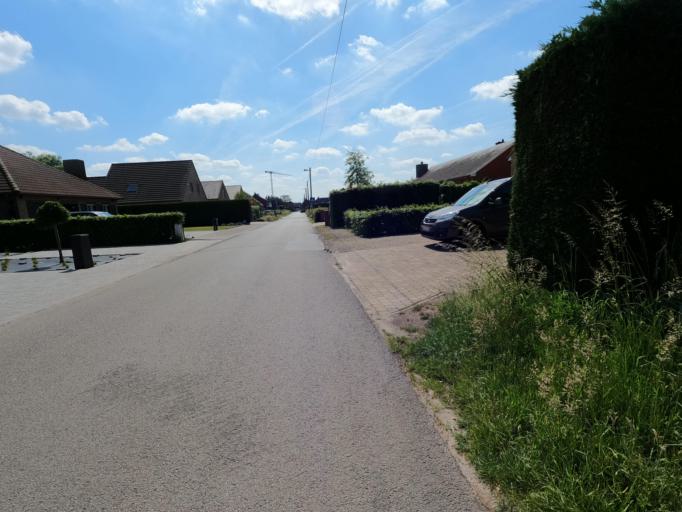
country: BE
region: Flanders
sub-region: Provincie Antwerpen
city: Schilde
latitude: 51.2666
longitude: 4.6279
